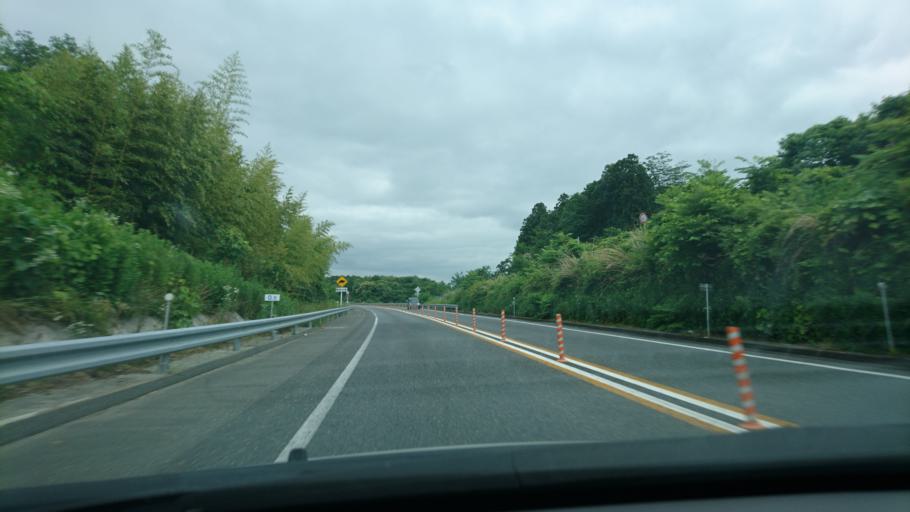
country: JP
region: Miyagi
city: Kogota
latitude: 38.7276
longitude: 141.0643
